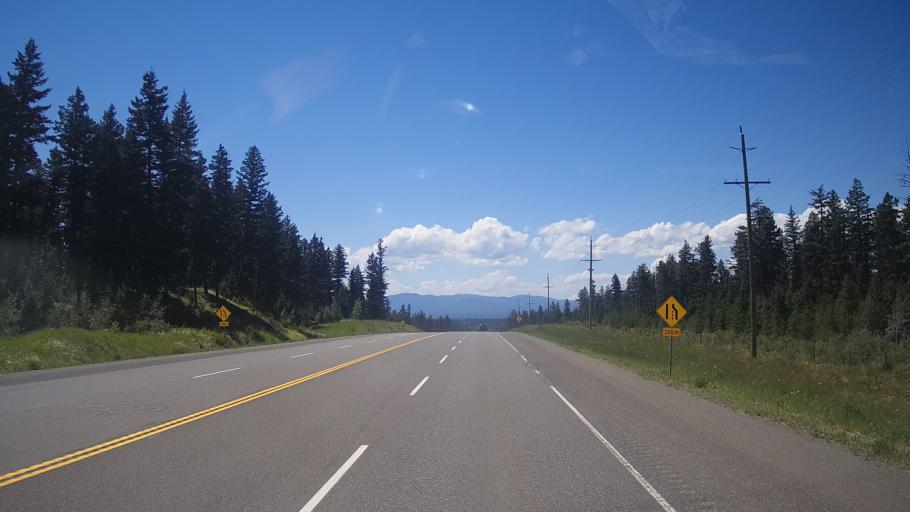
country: CA
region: British Columbia
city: Cache Creek
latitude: 51.2702
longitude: -121.4485
